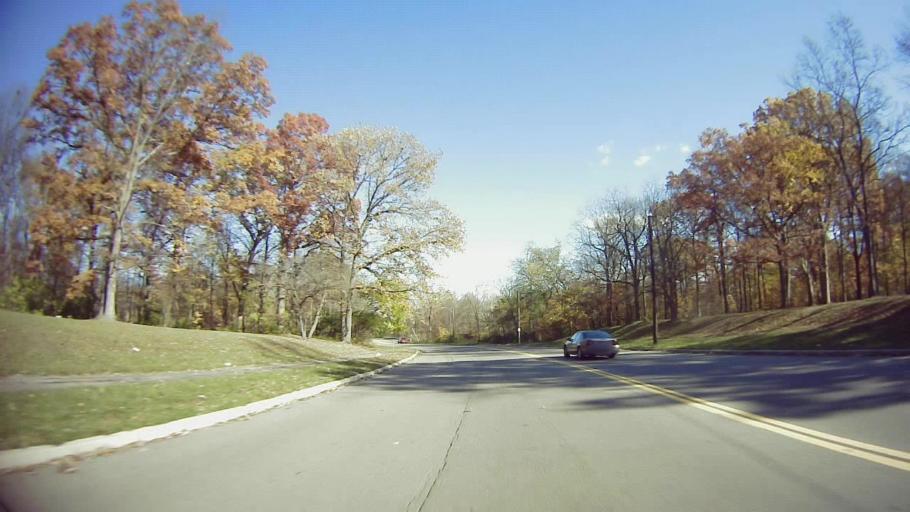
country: US
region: Michigan
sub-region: Wayne County
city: Dearborn Heights
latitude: 42.3521
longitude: -83.2524
